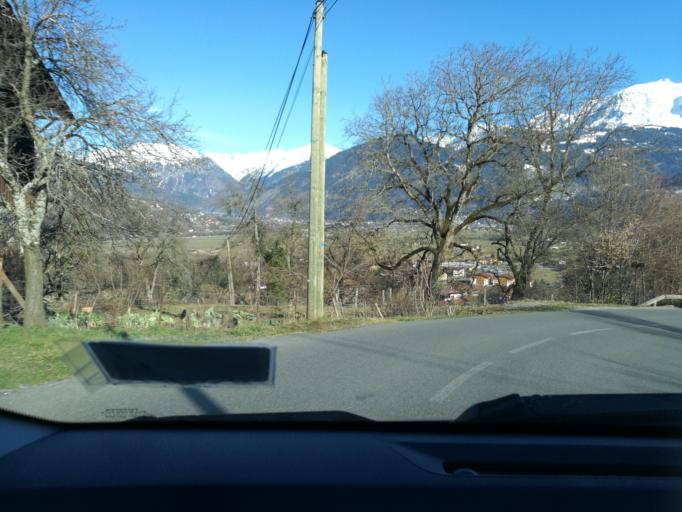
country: FR
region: Rhone-Alpes
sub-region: Departement de la Haute-Savoie
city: Domancy
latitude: 45.9125
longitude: 6.6470
